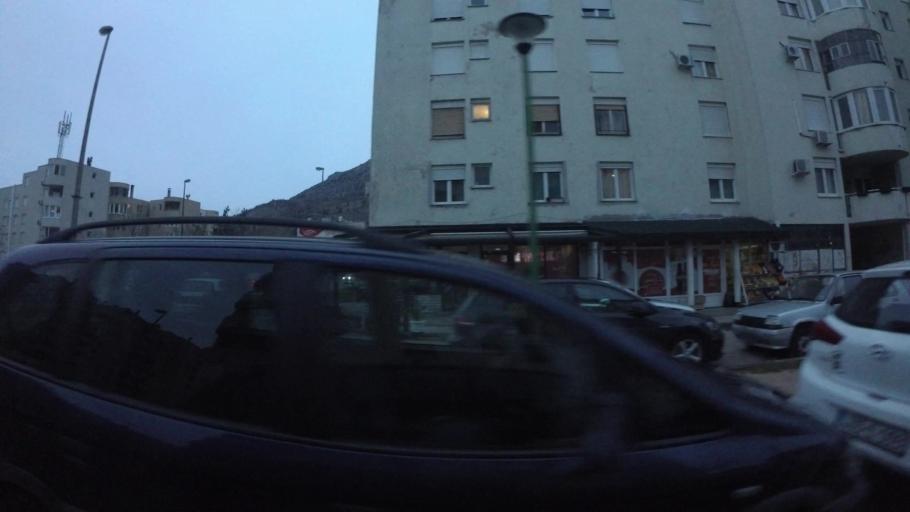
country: BA
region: Federation of Bosnia and Herzegovina
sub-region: Hercegovacko-Bosanski Kanton
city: Mostar
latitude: 43.3272
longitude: 17.8204
